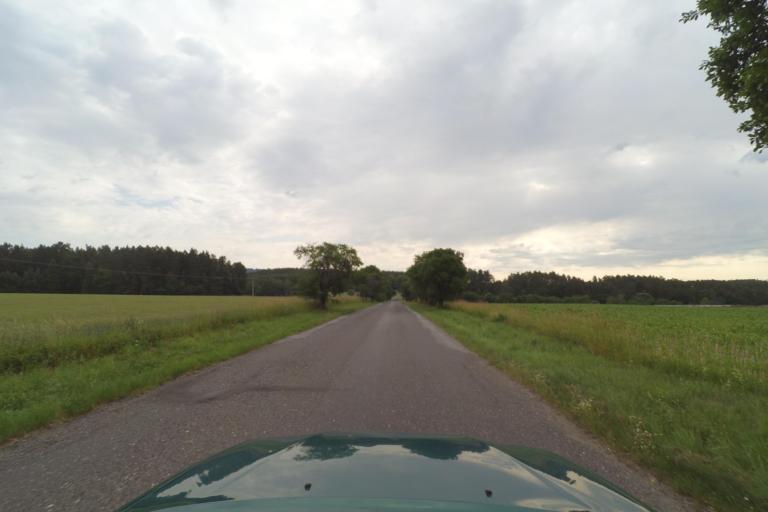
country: CZ
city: Cesky Dub
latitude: 50.6720
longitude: 15.0337
